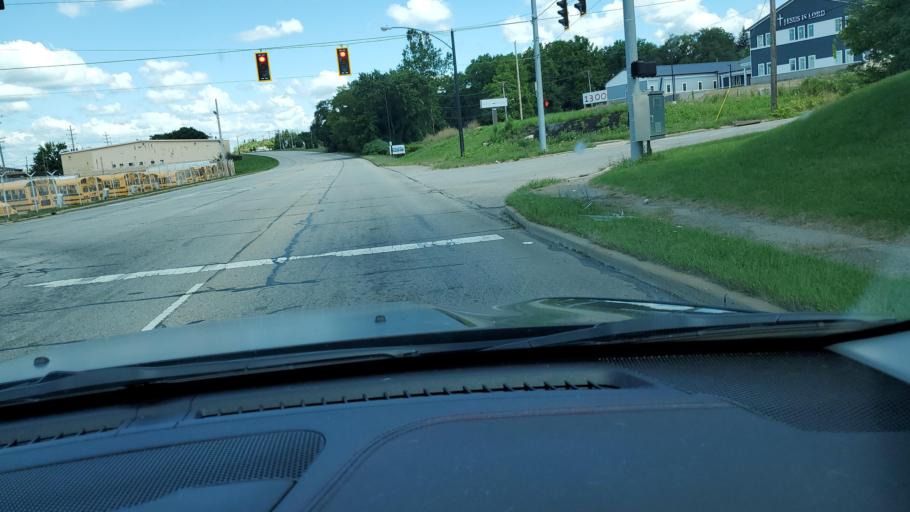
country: US
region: Ohio
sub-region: Mahoning County
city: Youngstown
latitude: 41.1139
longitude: -80.6678
